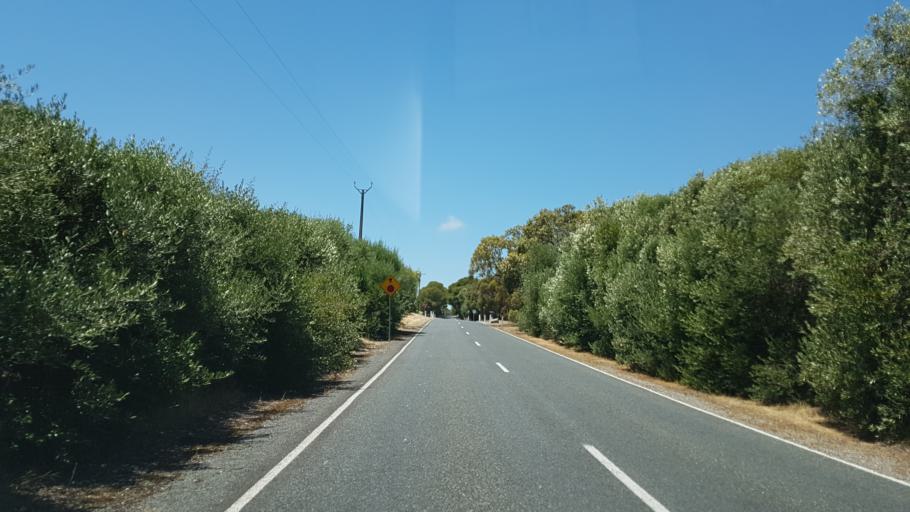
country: AU
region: South Australia
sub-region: Onkaparinga
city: McLaren Vale
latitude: -35.2319
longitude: 138.5048
